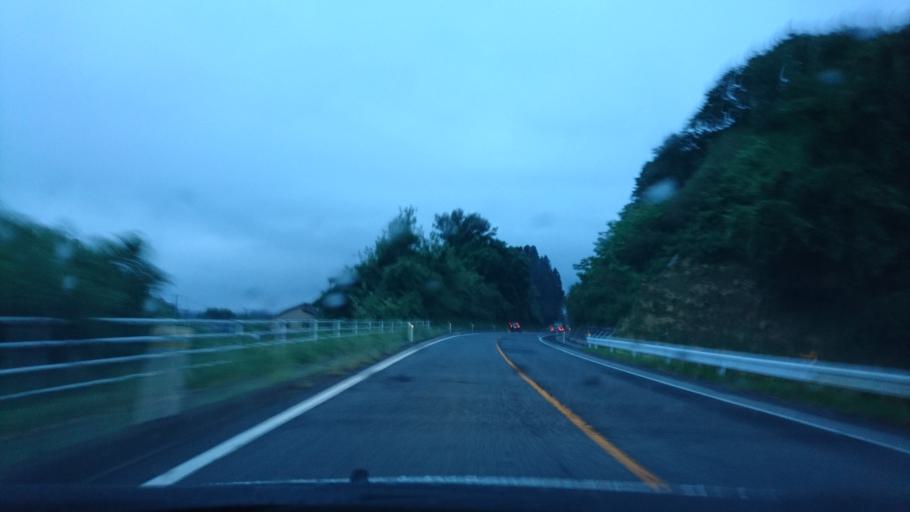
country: JP
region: Iwate
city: Ichinoseki
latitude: 38.7828
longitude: 141.0475
